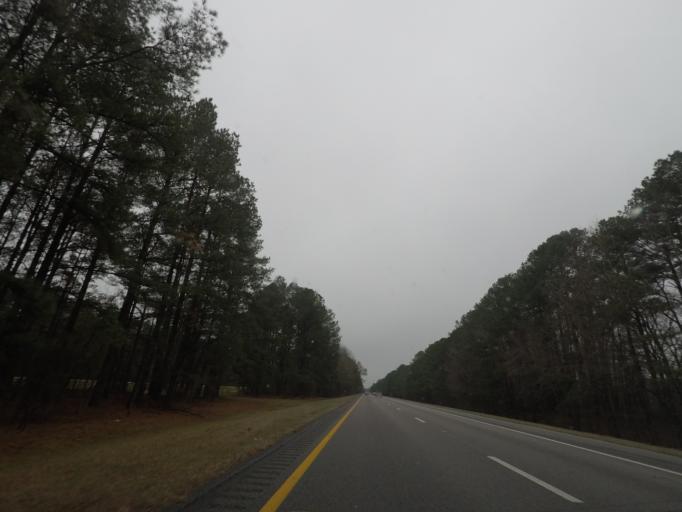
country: US
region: South Carolina
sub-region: Sumter County
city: East Sumter
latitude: 33.9254
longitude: -80.0747
